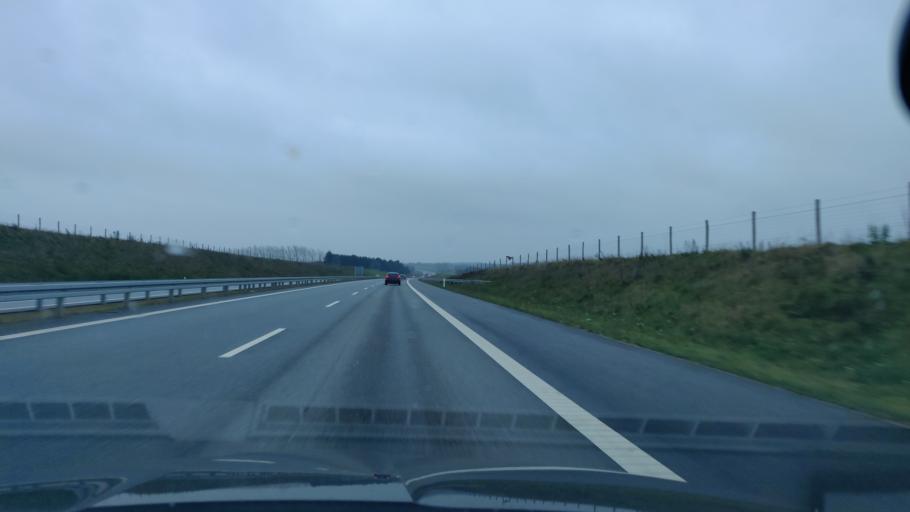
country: DK
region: Central Jutland
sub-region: Herning Kommune
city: Avlum
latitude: 56.2456
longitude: 8.7978
